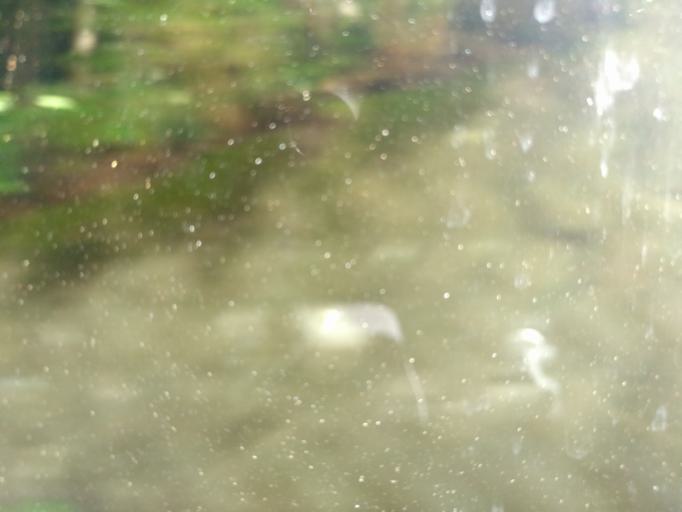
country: JP
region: Fukushima
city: Kitakata
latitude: 37.3772
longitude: 139.8377
